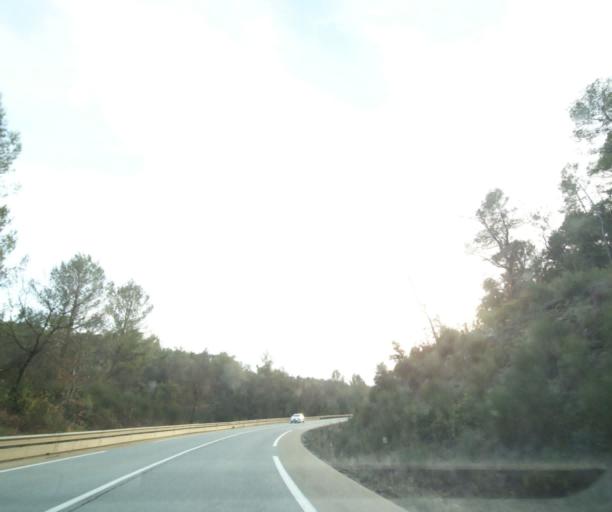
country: FR
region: Provence-Alpes-Cote d'Azur
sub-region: Departement du Var
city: La Motte
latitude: 43.5206
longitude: 6.5257
